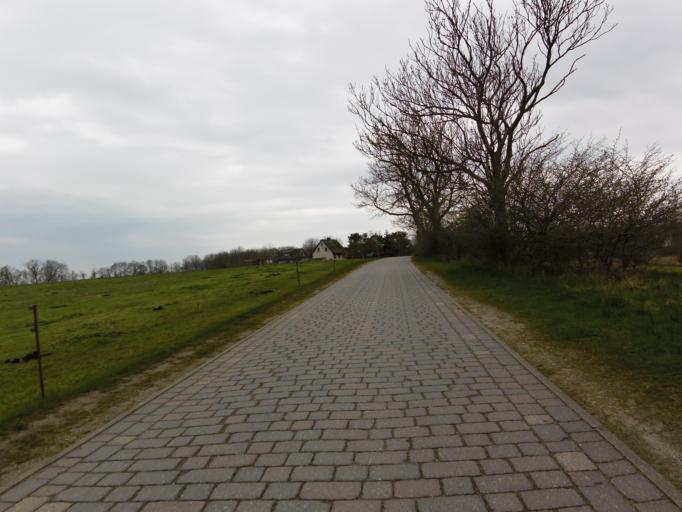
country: DE
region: Mecklenburg-Vorpommern
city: Hiddensee
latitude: 54.5879
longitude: 13.1174
